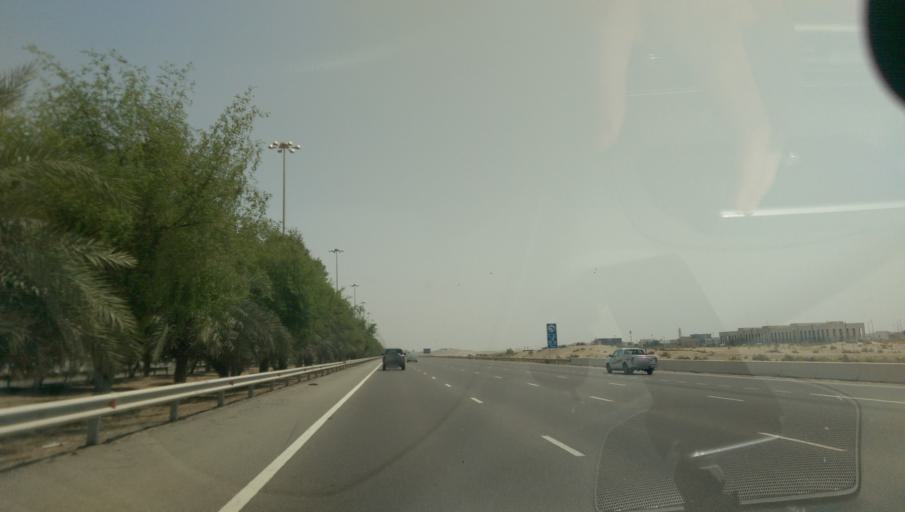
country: AE
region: Abu Dhabi
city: Abu Dhabi
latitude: 24.3726
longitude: 54.6560
